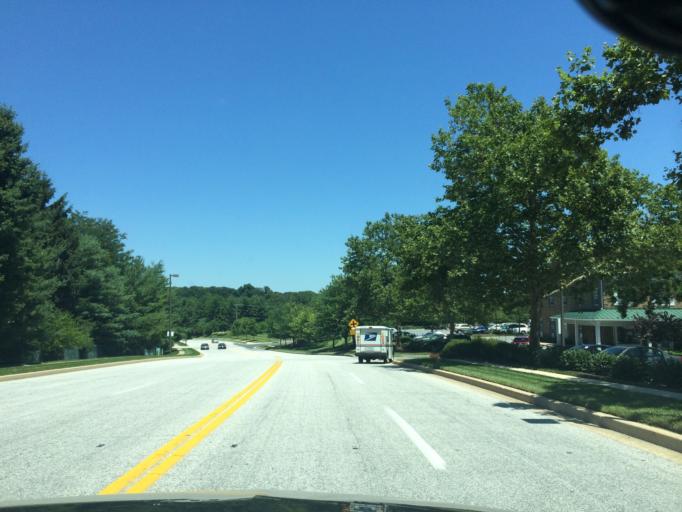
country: US
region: Maryland
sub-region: Baltimore County
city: Garrison
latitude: 39.3978
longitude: -76.7486
